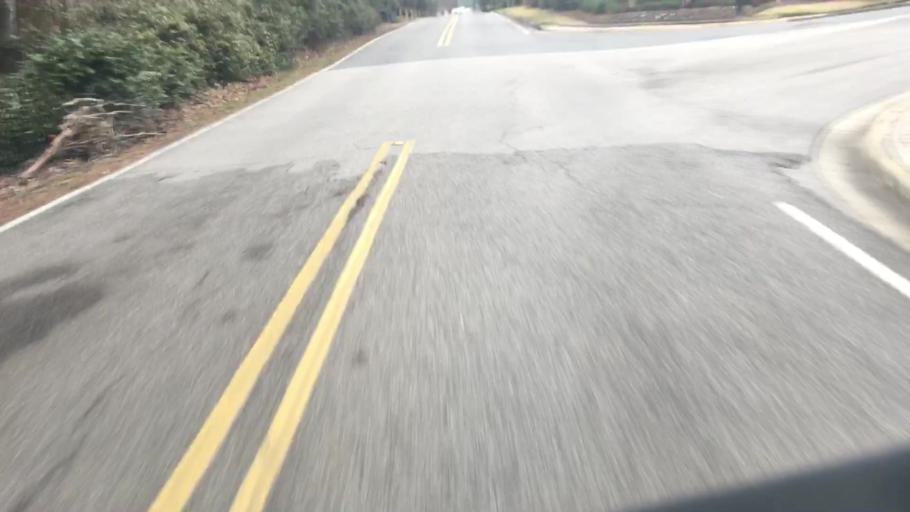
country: US
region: Alabama
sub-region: Jefferson County
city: Vestavia Hills
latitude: 33.4205
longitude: -86.7592
